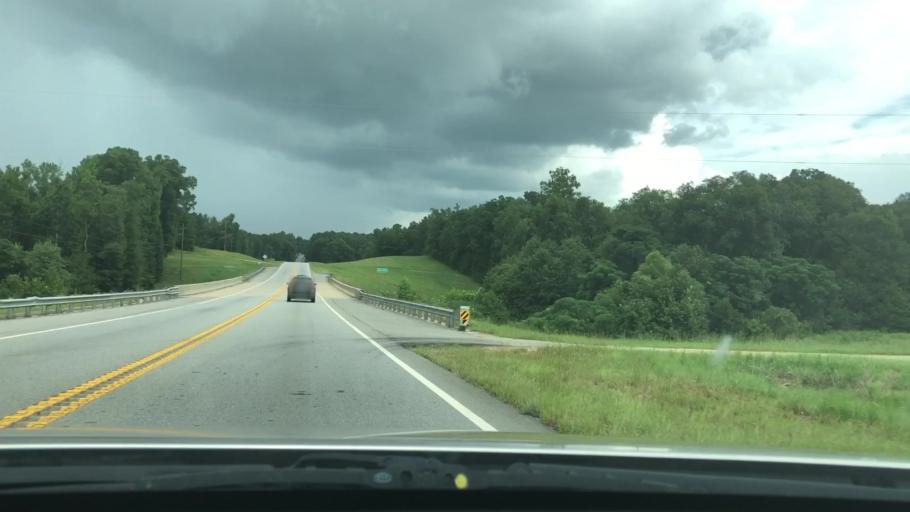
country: US
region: Georgia
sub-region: Lamar County
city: Barnesville
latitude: 33.1832
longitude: -84.0798
